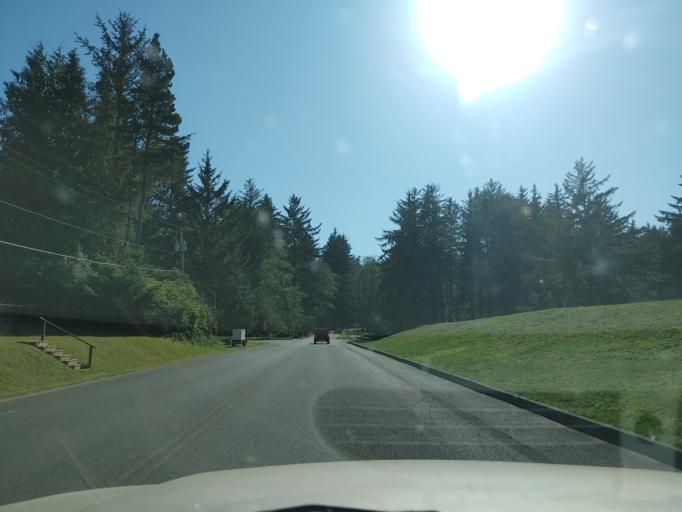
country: US
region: Oregon
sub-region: Clatsop County
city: Warrenton
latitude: 46.1820
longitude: -123.9620
